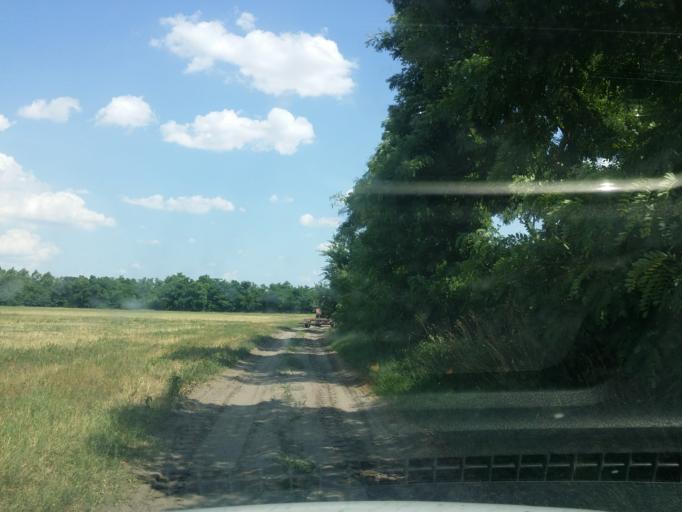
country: HU
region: Bacs-Kiskun
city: Jaszszentlaszlo
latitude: 46.5714
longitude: 19.7768
